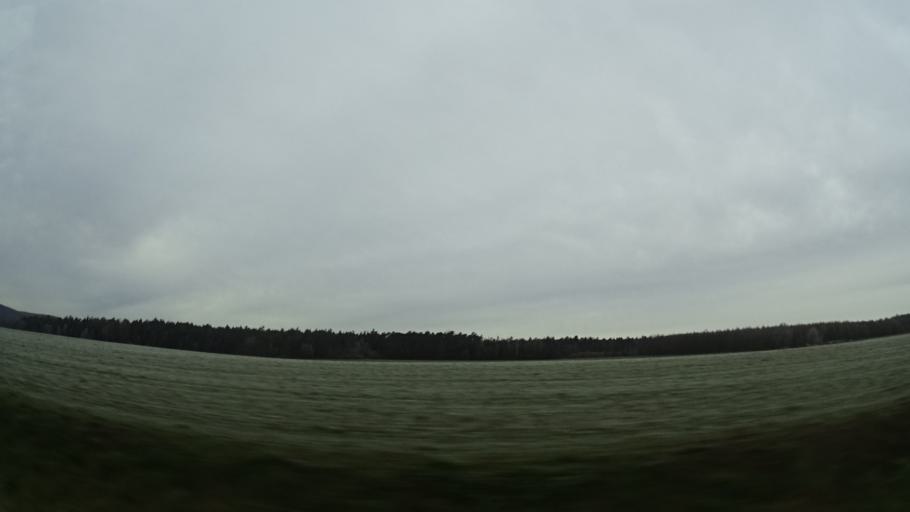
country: DE
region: Thuringia
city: Buttlar
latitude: 50.7711
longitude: 9.9672
